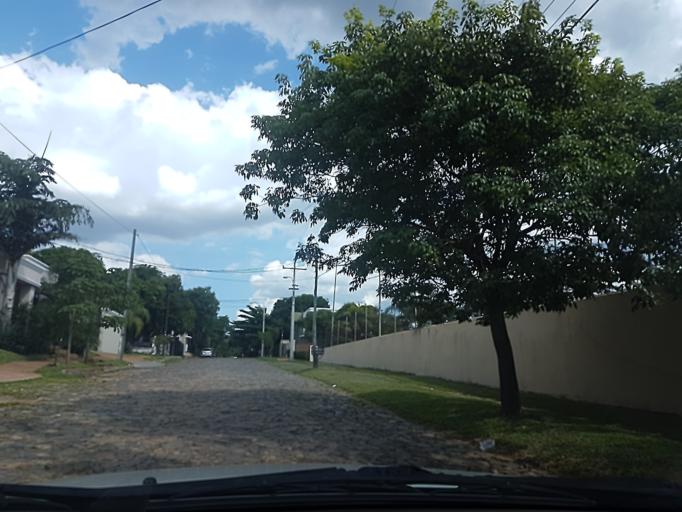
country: PY
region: Asuncion
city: Asuncion
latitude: -25.2634
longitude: -57.5768
